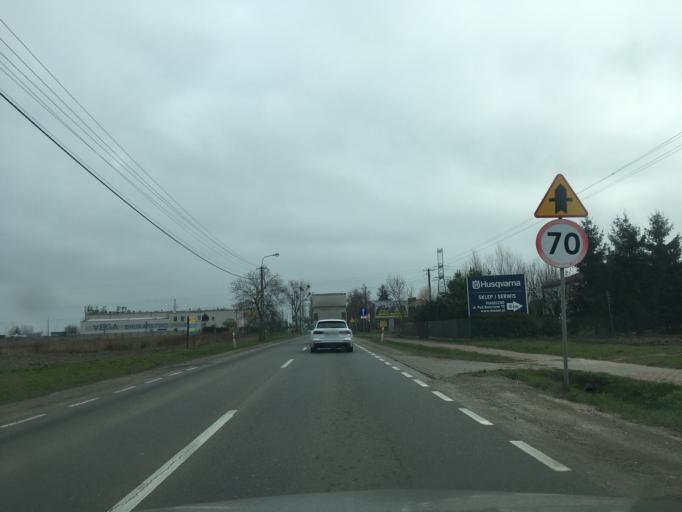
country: PL
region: Masovian Voivodeship
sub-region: Powiat piaseczynski
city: Lesznowola
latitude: 52.0822
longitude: 20.9643
